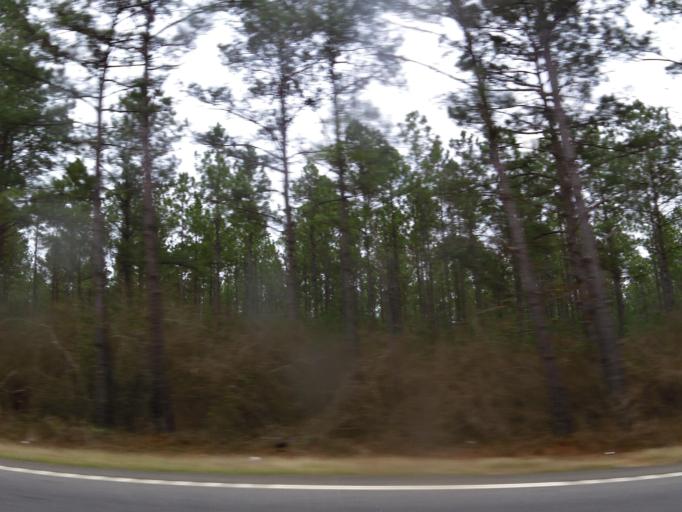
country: US
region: Georgia
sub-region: Randolph County
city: Shellman
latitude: 31.7785
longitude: -84.5785
